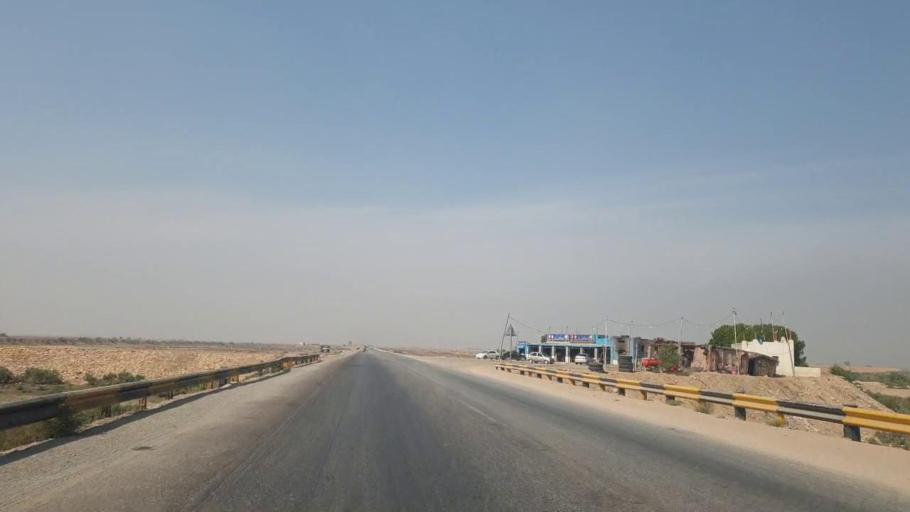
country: PK
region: Sindh
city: Hala
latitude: 25.8813
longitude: 68.2472
